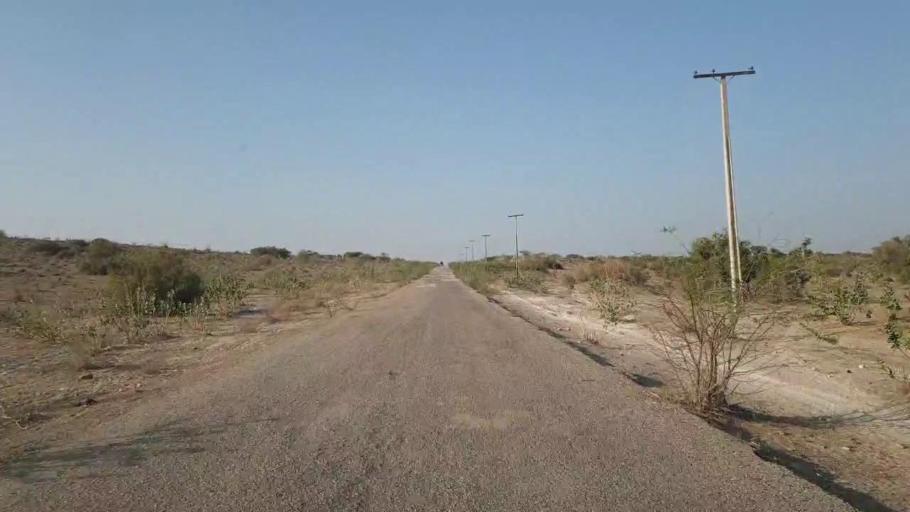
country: PK
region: Sindh
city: Chor
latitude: 25.6069
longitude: 69.8377
